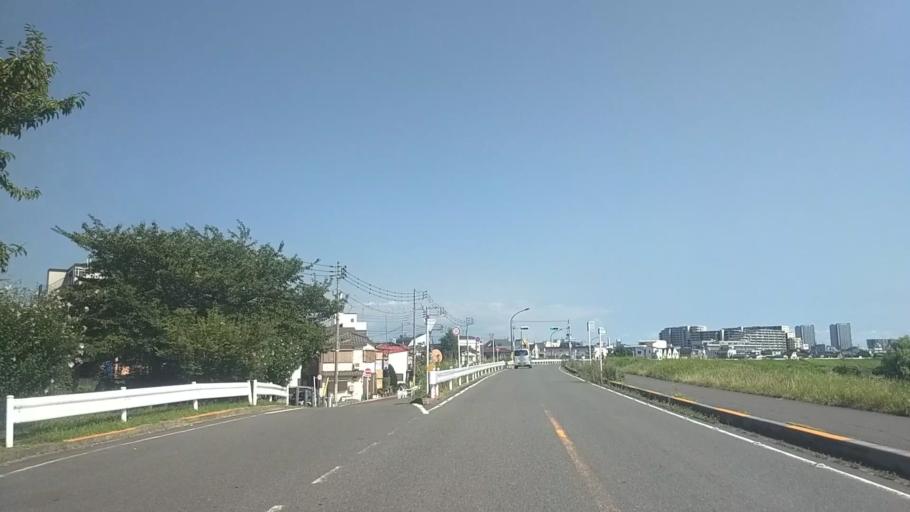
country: JP
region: Kanagawa
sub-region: Kawasaki-shi
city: Kawasaki
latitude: 35.5543
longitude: 139.7032
